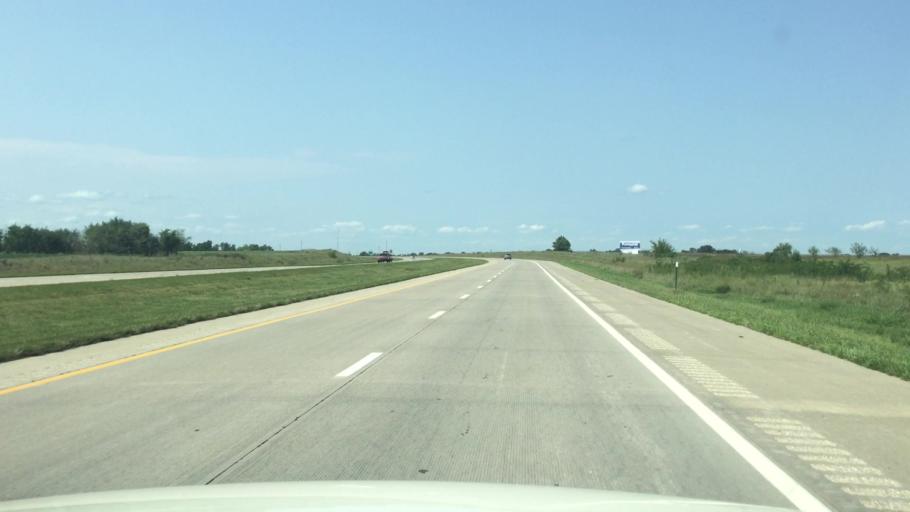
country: US
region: Kansas
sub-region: Linn County
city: Pleasanton
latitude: 38.1700
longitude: -94.6958
